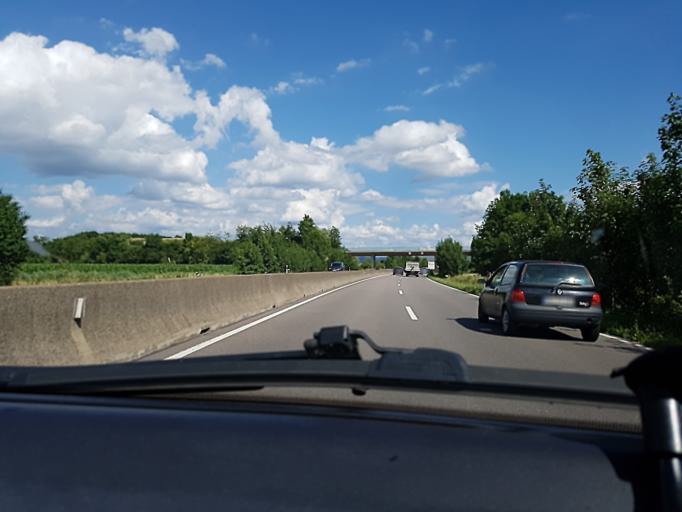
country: DE
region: Baden-Wuerttemberg
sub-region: Freiburg Region
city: Willstatt
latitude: 48.5444
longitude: 7.8995
